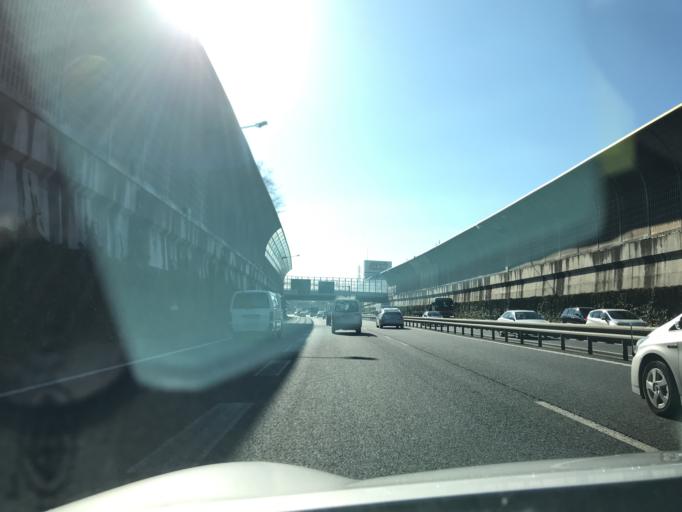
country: JP
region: Chiba
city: Chiba
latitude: 35.6468
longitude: 140.1098
